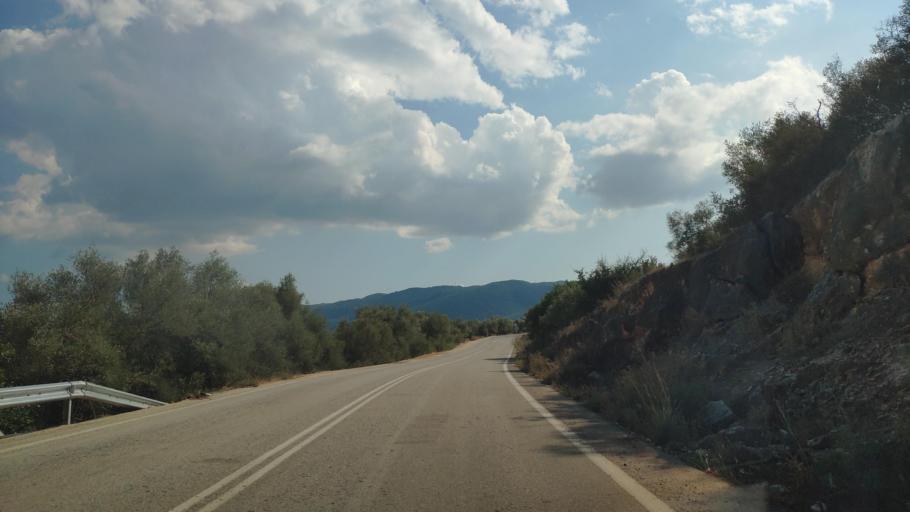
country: GR
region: West Greece
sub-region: Nomos Aitolias kai Akarnanias
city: Stanos
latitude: 38.7765
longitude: 21.1846
